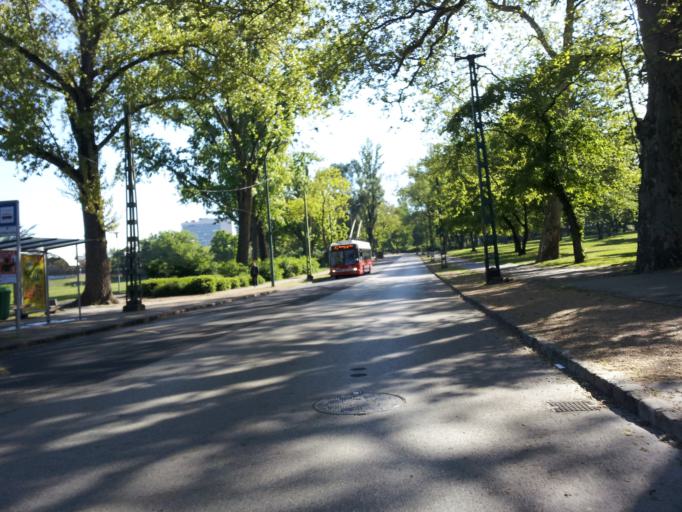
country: HU
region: Budapest
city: Budapest XIII. keruelet
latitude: 47.5124
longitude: 19.0853
